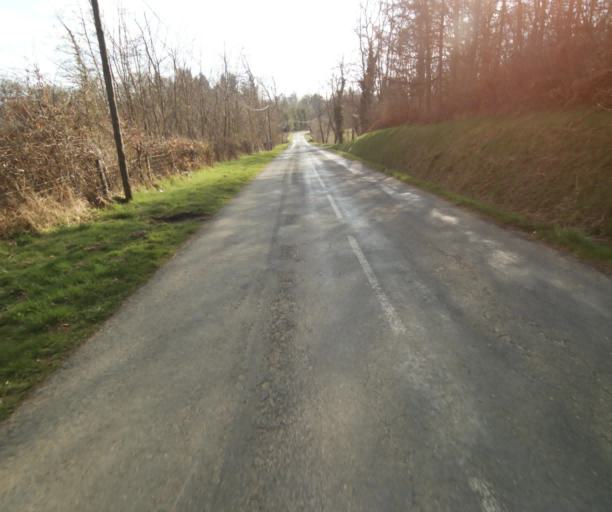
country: FR
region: Limousin
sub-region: Departement de la Correze
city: Saint-Clement
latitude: 45.3450
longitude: 1.6236
